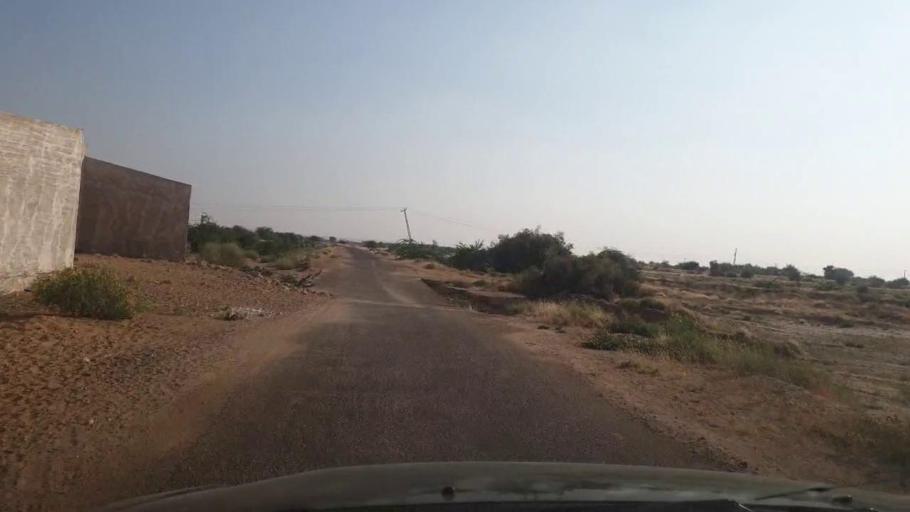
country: PK
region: Sindh
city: Jamshoro
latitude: 25.3470
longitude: 67.8381
